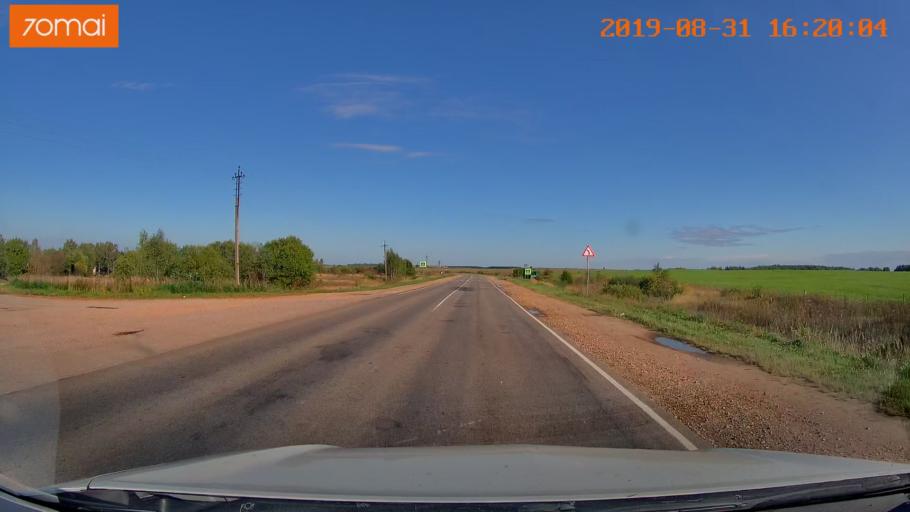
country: RU
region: Kaluga
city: Babynino
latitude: 54.5245
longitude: 35.5946
